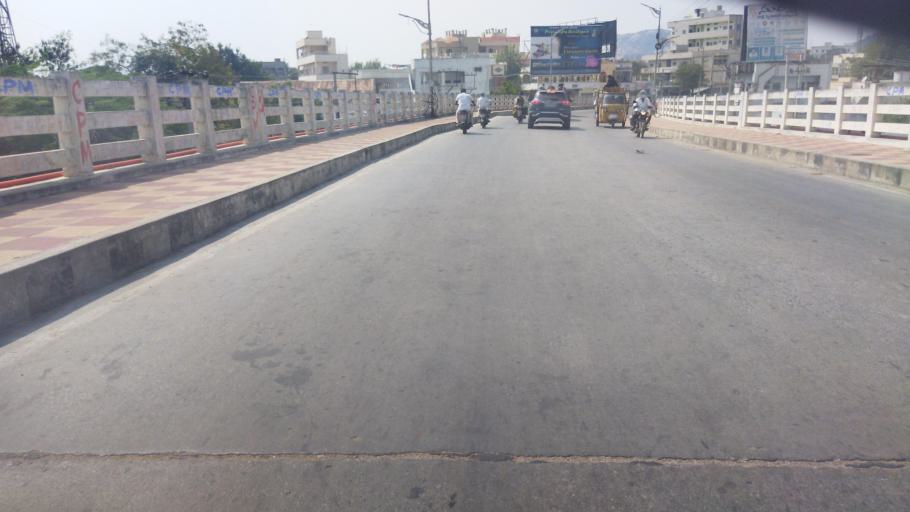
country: IN
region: Telangana
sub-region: Nalgonda
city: Nalgonda
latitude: 17.0647
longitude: 79.2794
